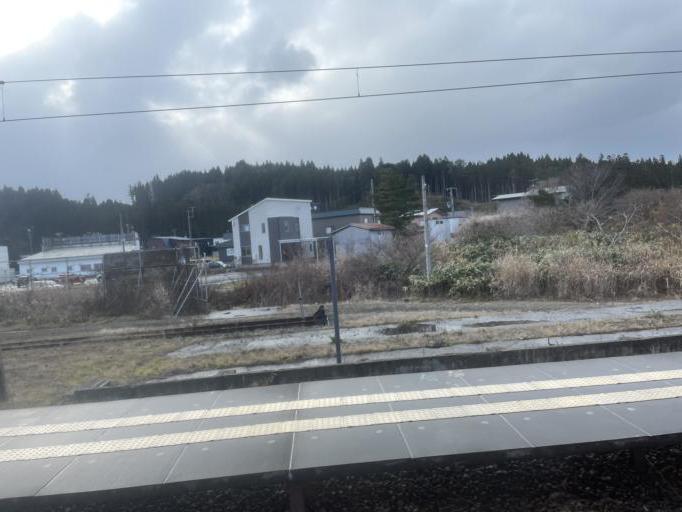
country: JP
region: Aomori
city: Aomori Shi
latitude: 41.0391
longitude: 140.6417
